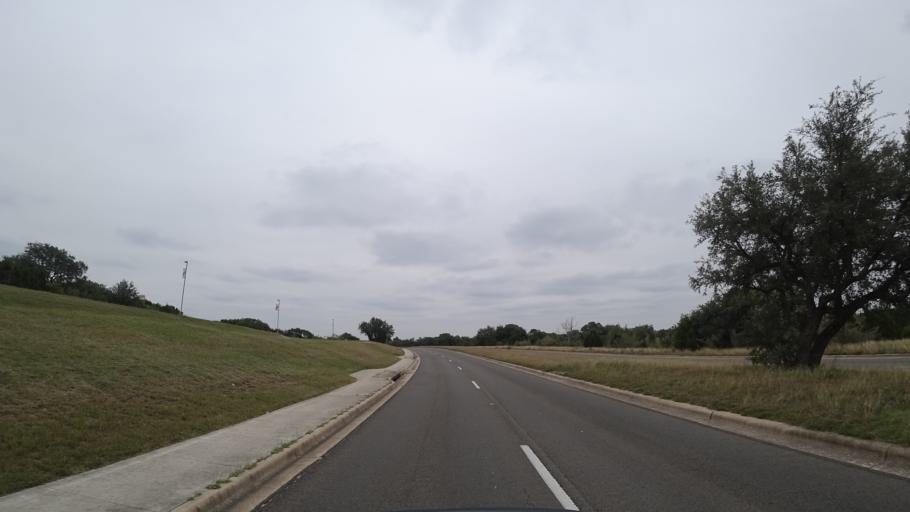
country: US
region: Texas
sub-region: Travis County
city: Shady Hollow
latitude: 30.2130
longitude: -97.8930
